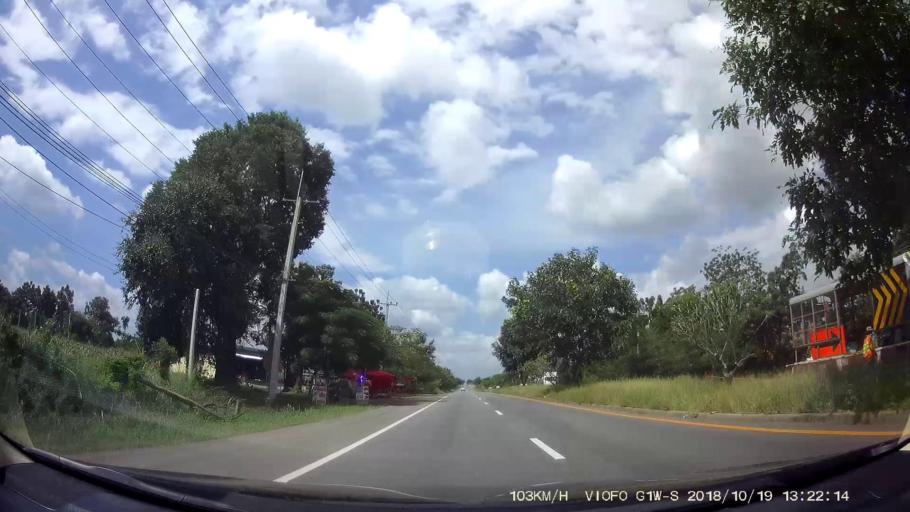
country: TH
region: Chaiyaphum
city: Chatturat
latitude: 15.4742
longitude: 101.8241
